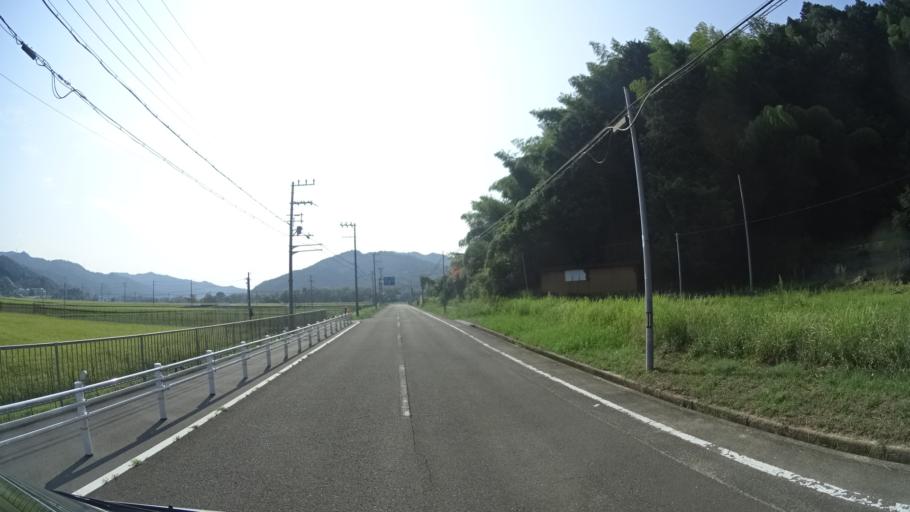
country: JP
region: Kyoto
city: Maizuru
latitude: 35.4331
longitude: 135.2618
